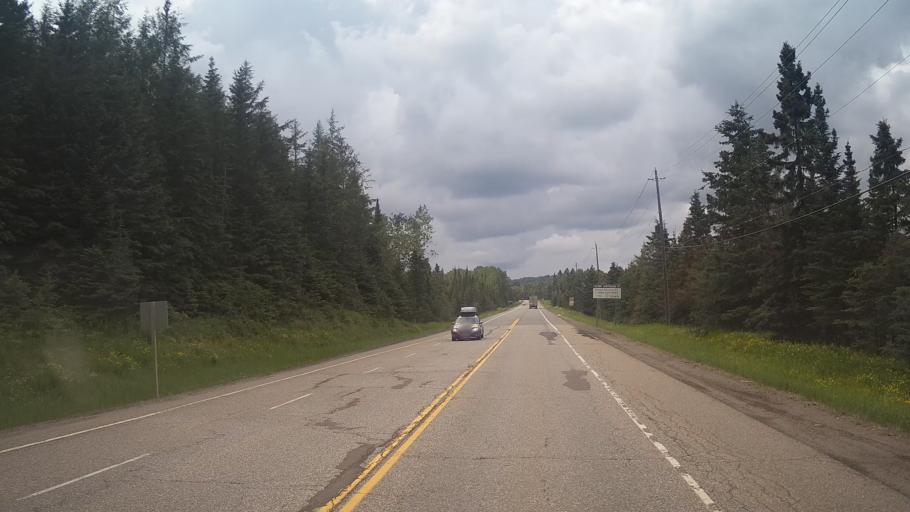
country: CA
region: Ontario
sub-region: Thunder Bay District
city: Thunder Bay
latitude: 48.4832
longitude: -89.3276
